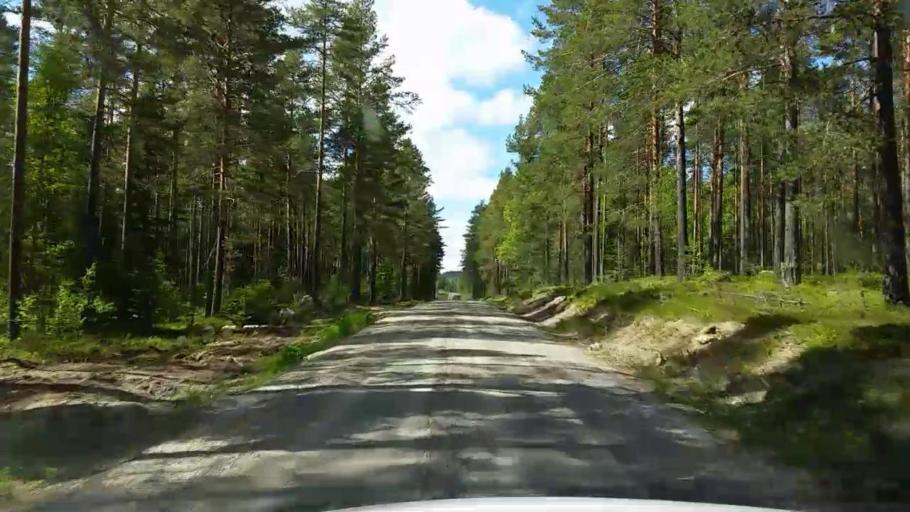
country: SE
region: Gaevleborg
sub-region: Ovanakers Kommun
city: Edsbyn
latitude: 61.5757
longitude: 15.9107
